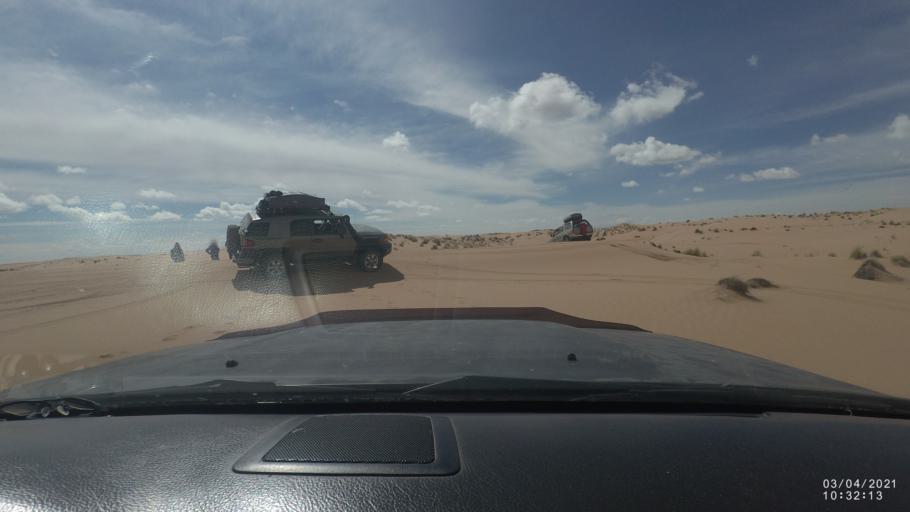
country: BO
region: Oruro
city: Poopo
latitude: -18.7055
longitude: -67.5217
